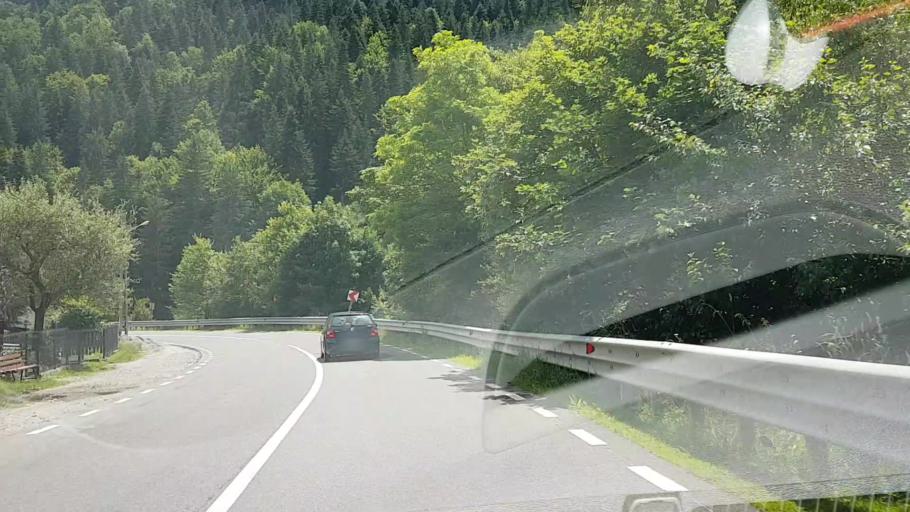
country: RO
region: Suceava
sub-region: Comuna Brosteni
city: Brosteni
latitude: 47.2570
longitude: 25.6699
